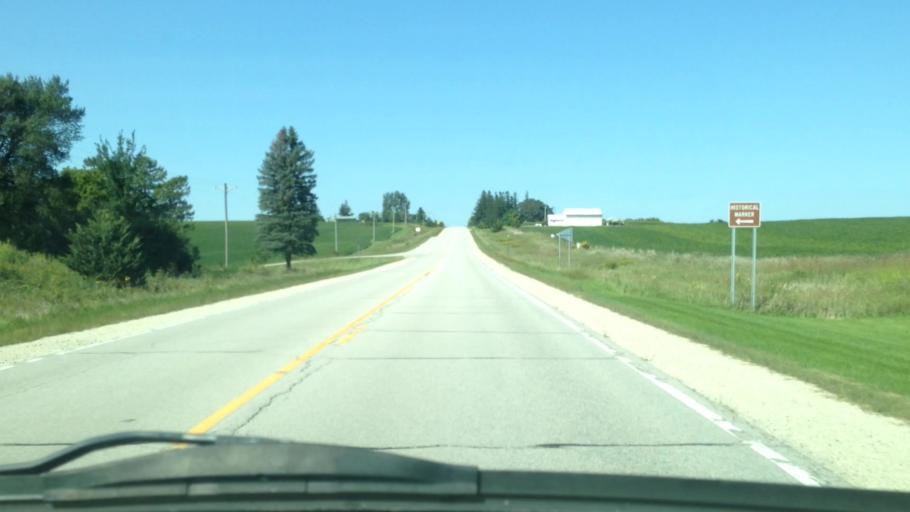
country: US
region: Minnesota
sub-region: Houston County
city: Spring Grove
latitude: 43.6150
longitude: -91.7904
